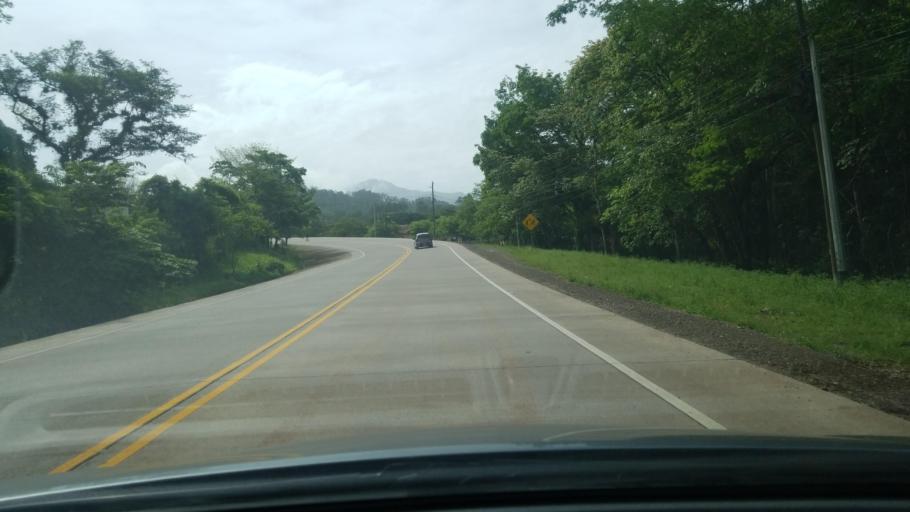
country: HN
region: Copan
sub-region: Santa Rita
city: Santa Rita, Copan
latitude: 14.8699
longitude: -89.0611
